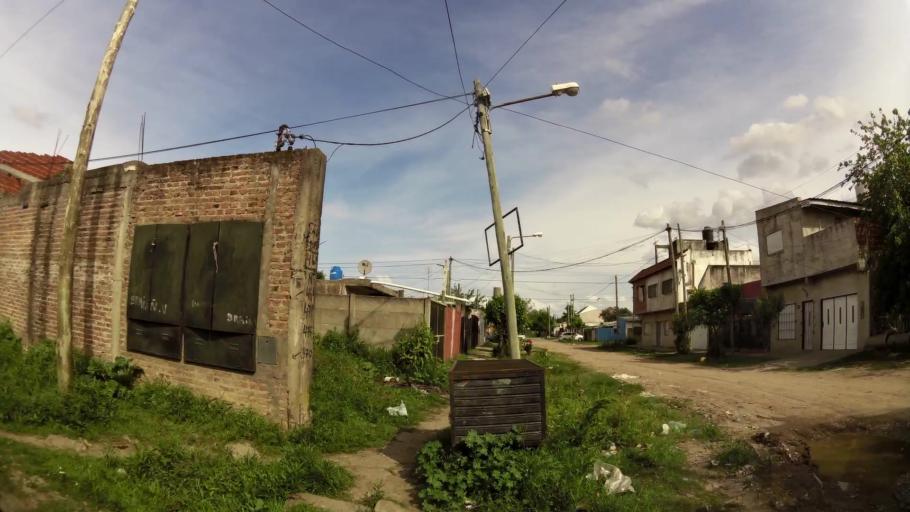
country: AR
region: Buenos Aires
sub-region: Partido de Quilmes
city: Quilmes
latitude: -34.7745
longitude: -58.2570
